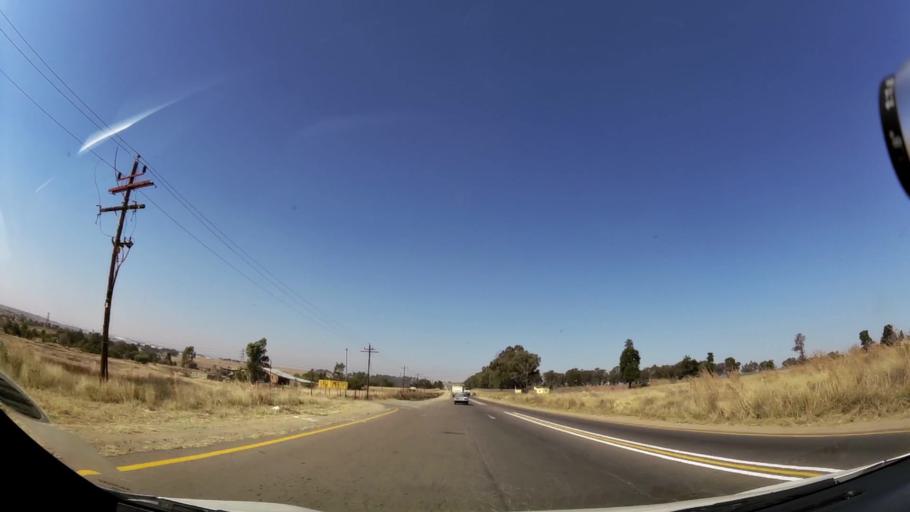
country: ZA
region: Gauteng
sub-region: City of Johannesburg Metropolitan Municipality
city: Diepsloot
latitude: -25.9329
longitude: 28.0826
